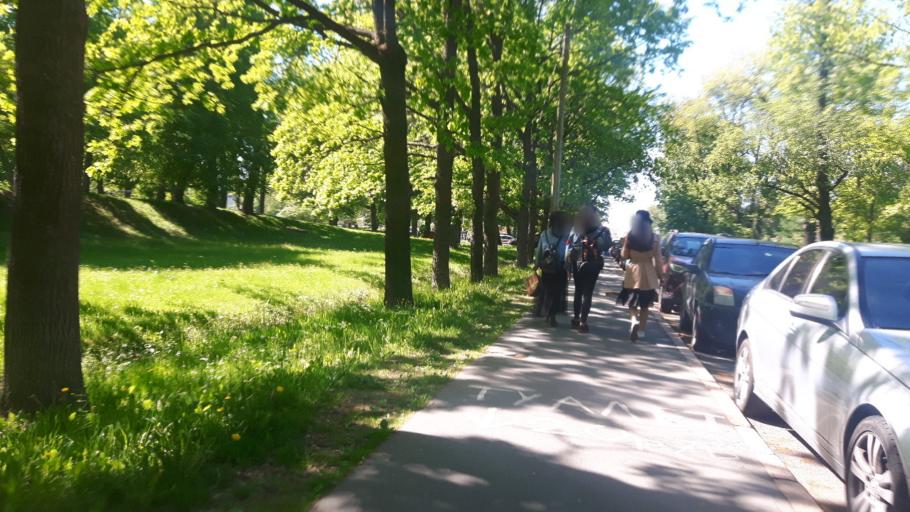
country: RU
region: St.-Petersburg
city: Peterhof
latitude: 59.8821
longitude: 29.9176
